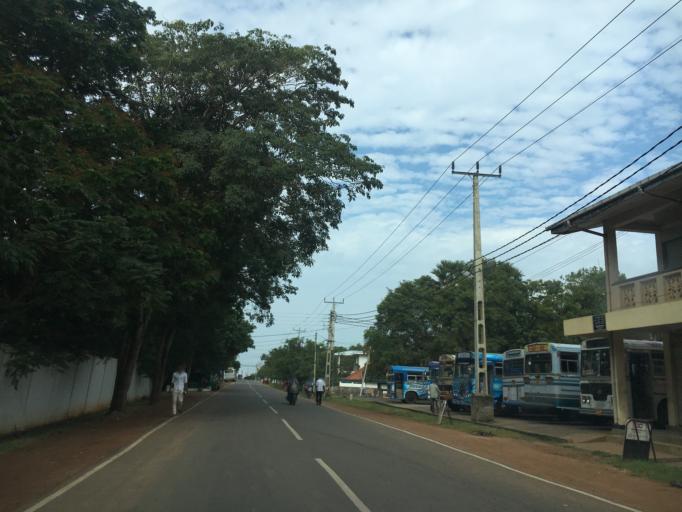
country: LK
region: North Western
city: Puttalam
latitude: 8.0276
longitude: 79.8335
